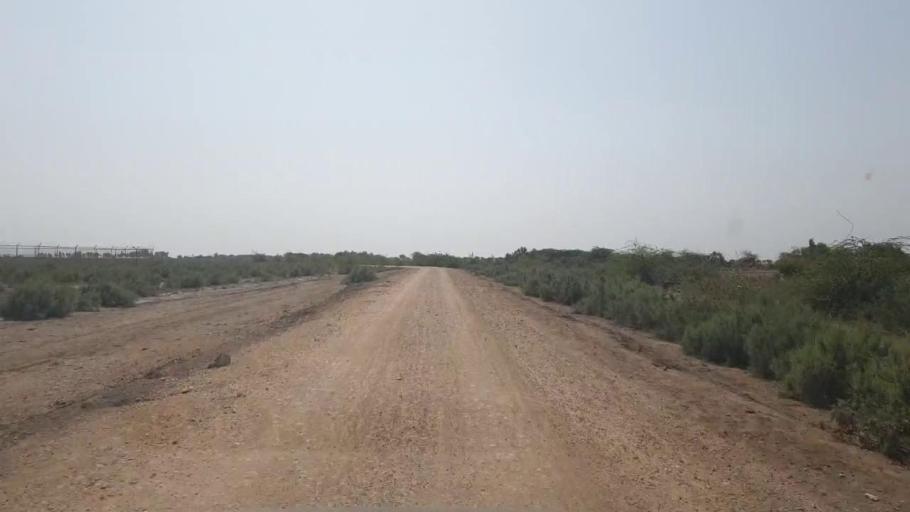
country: PK
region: Sindh
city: Jati
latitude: 24.3864
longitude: 68.5987
